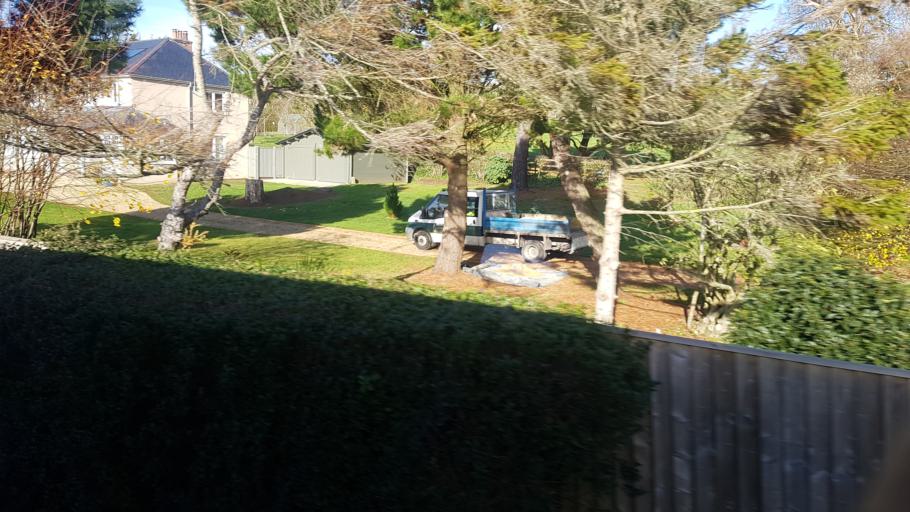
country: GB
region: England
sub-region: Isle of Wight
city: Chale
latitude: 50.6418
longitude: -1.3692
